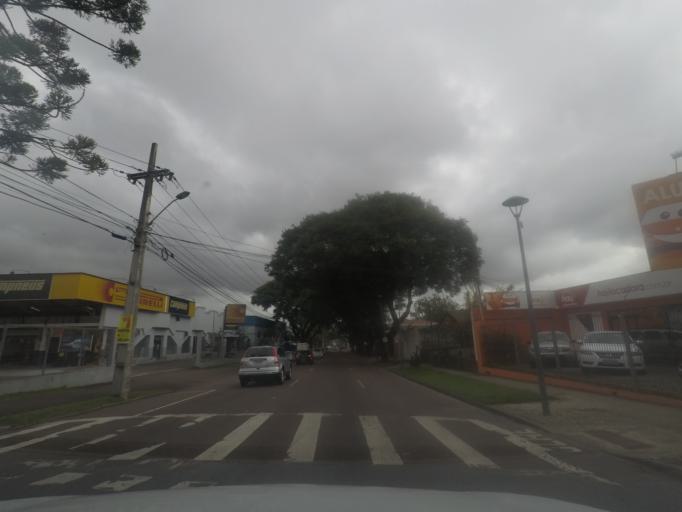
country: BR
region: Parana
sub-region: Curitiba
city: Curitiba
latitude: -25.4393
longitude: -49.2526
